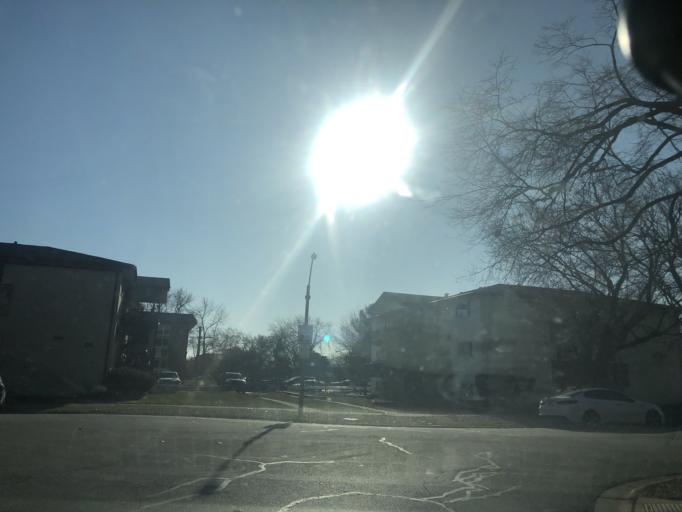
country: US
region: Illinois
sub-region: DuPage County
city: Addison
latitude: 41.9350
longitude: -88.0016
